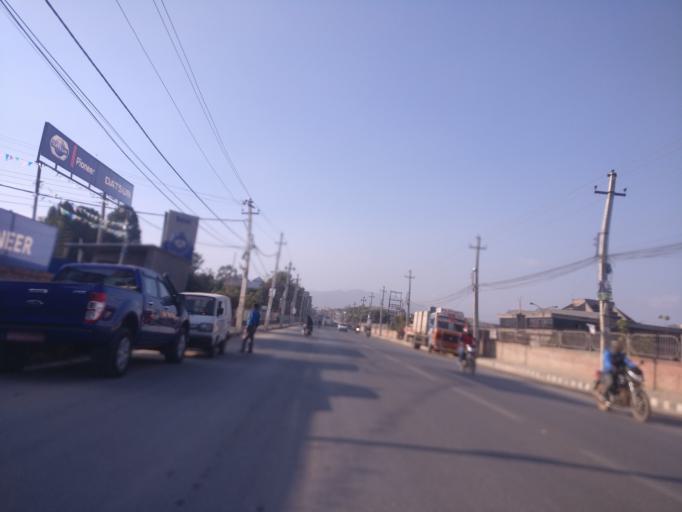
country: NP
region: Central Region
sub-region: Bagmati Zone
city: Patan
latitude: 27.6550
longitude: 85.3279
